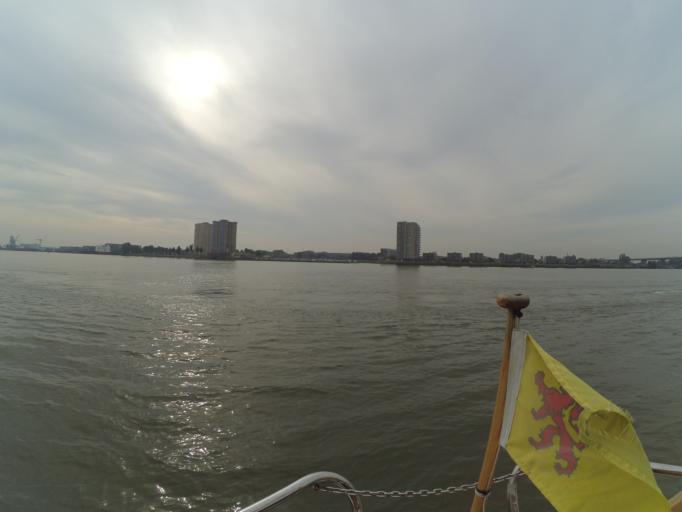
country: NL
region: South Holland
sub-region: Gemeente Capelle aan den IJssel
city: Capelle-West
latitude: 51.9064
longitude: 4.5555
